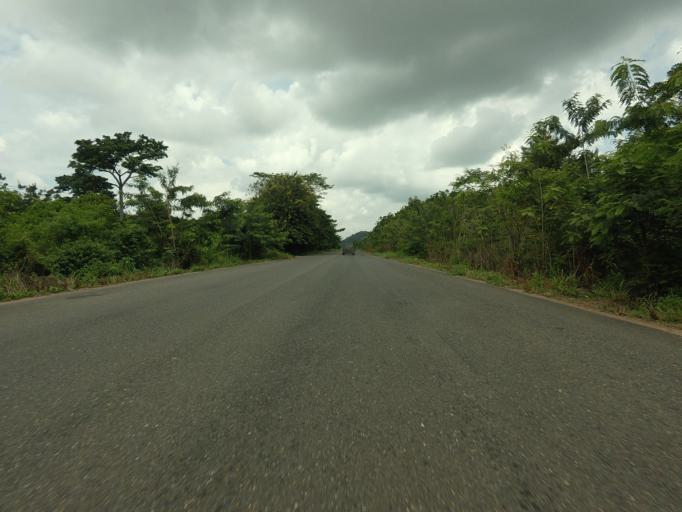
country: GH
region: Volta
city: Ho
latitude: 6.4404
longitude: 0.1727
